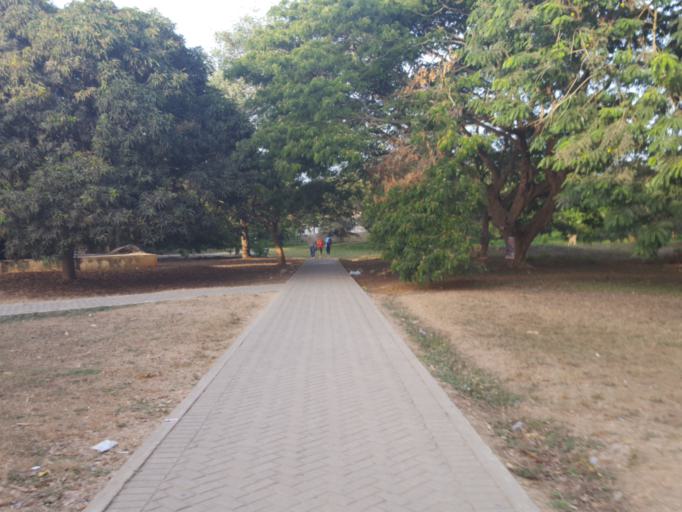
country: GH
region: Central
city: Cape Coast
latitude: 5.1168
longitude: -1.2911
